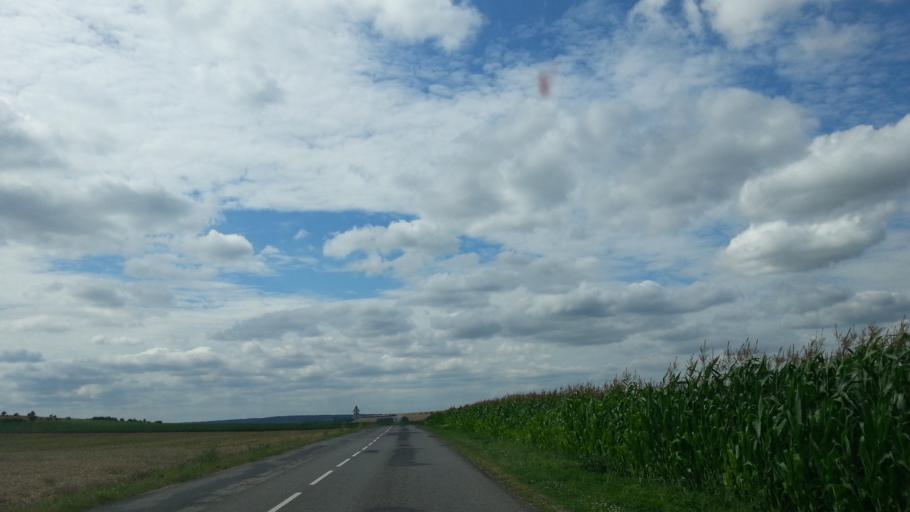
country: FR
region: Lorraine
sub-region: Departement de la Meuse
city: Belleville-sur-Meuse
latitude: 49.2068
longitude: 5.3533
